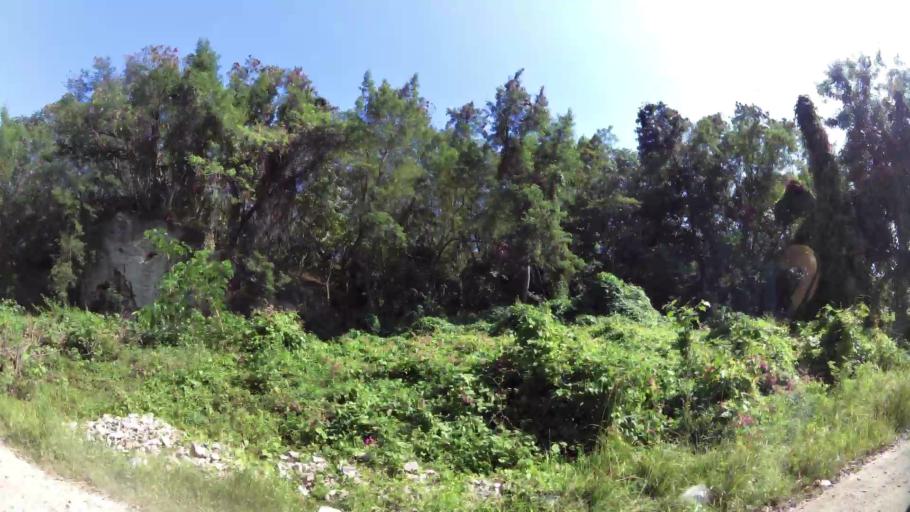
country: DO
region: Santo Domingo
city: Santo Domingo Oeste
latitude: 18.4743
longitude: -70.0070
